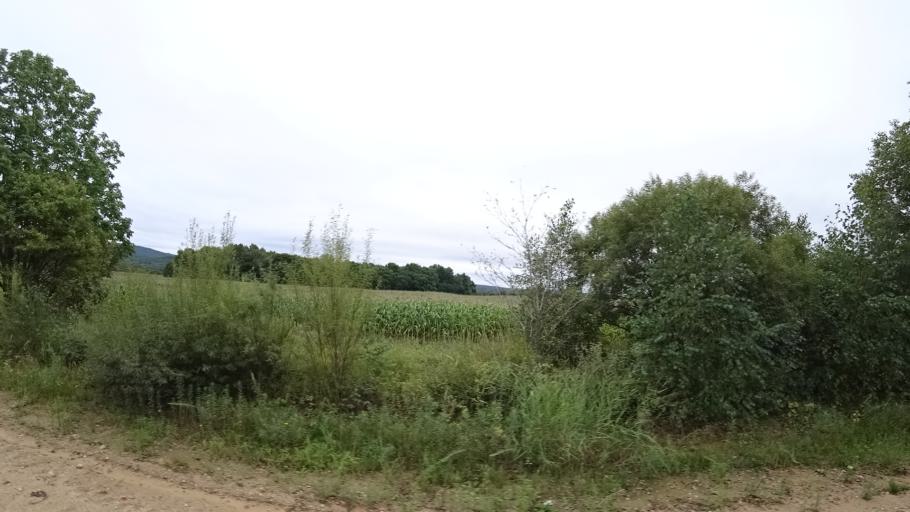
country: RU
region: Primorskiy
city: Rettikhovka
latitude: 44.1597
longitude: 132.6928
